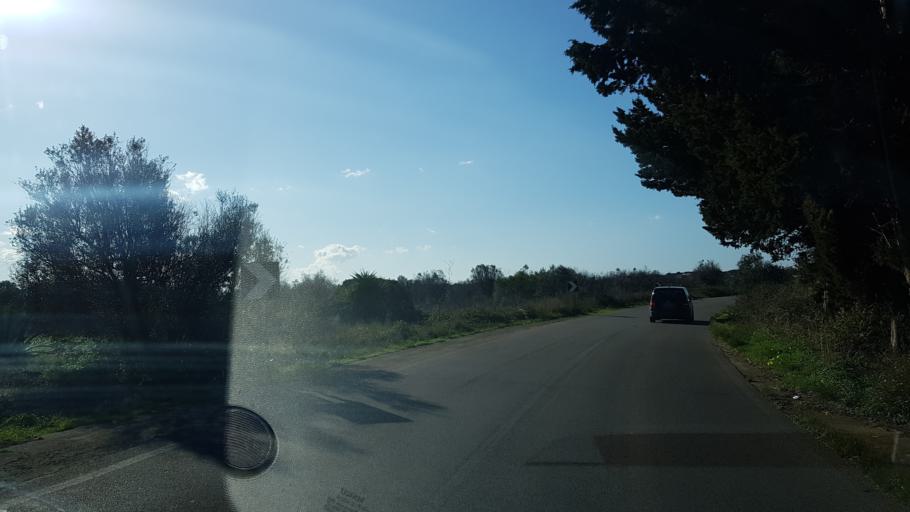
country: IT
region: Apulia
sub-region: Provincia di Lecce
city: Gallipoli
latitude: 40.0927
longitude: 18.0210
